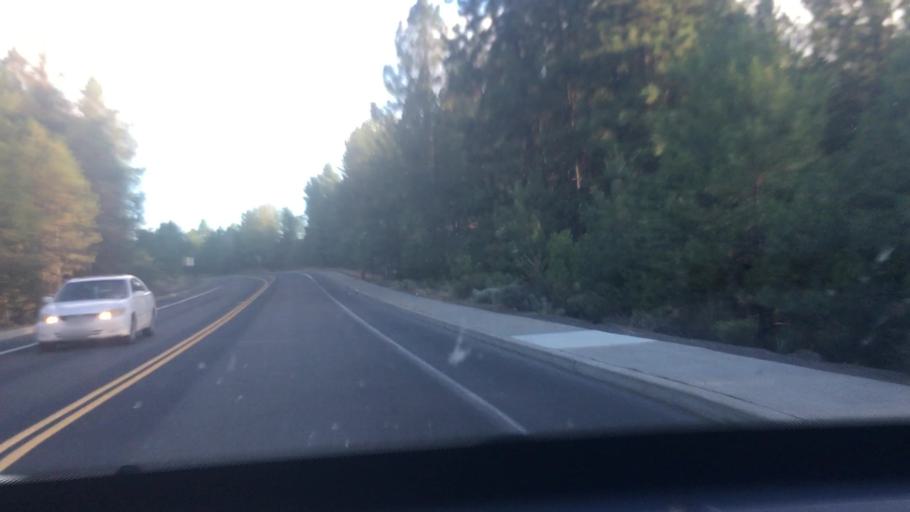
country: US
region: Oregon
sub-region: Deschutes County
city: Bend
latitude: 44.0443
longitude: -121.3441
